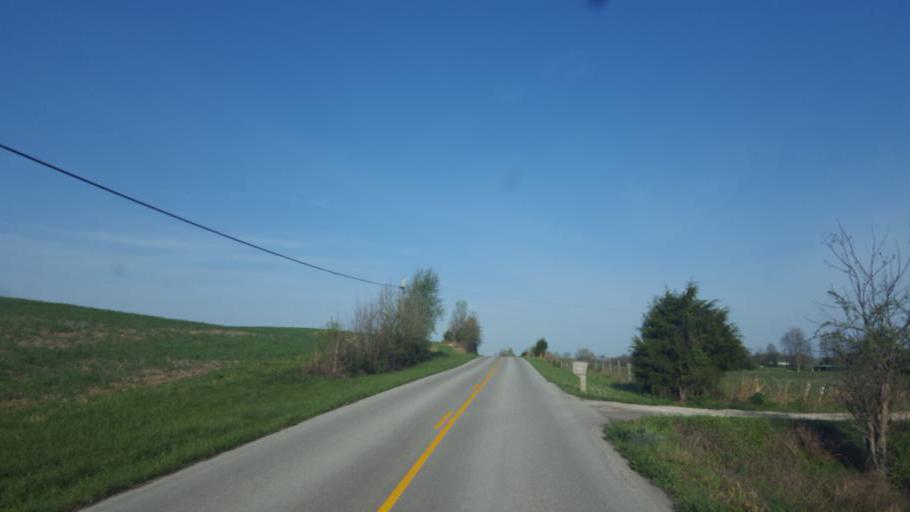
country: US
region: Kentucky
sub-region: Hardin County
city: Elizabethtown
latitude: 37.4952
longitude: -85.9549
